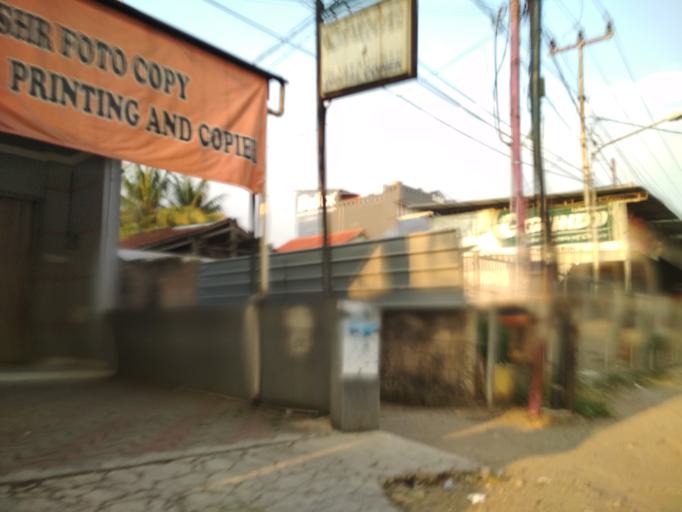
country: ID
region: West Java
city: Ciampea
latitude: -6.5626
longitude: 106.7171
